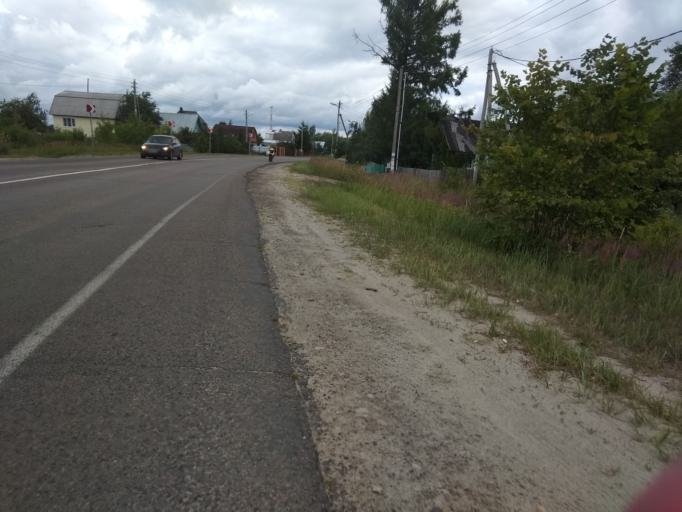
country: RU
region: Moskovskaya
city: Kerva
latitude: 55.5920
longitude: 39.7008
